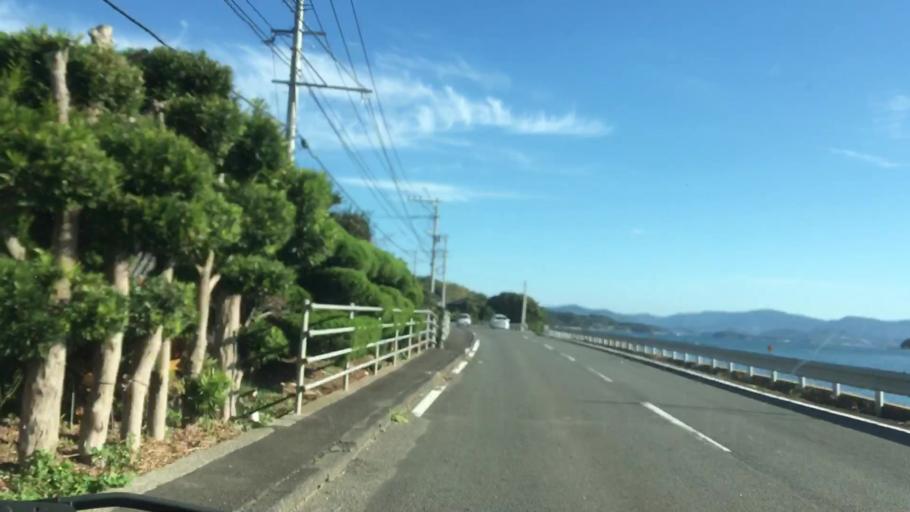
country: JP
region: Nagasaki
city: Sasebo
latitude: 33.0235
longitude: 129.7385
